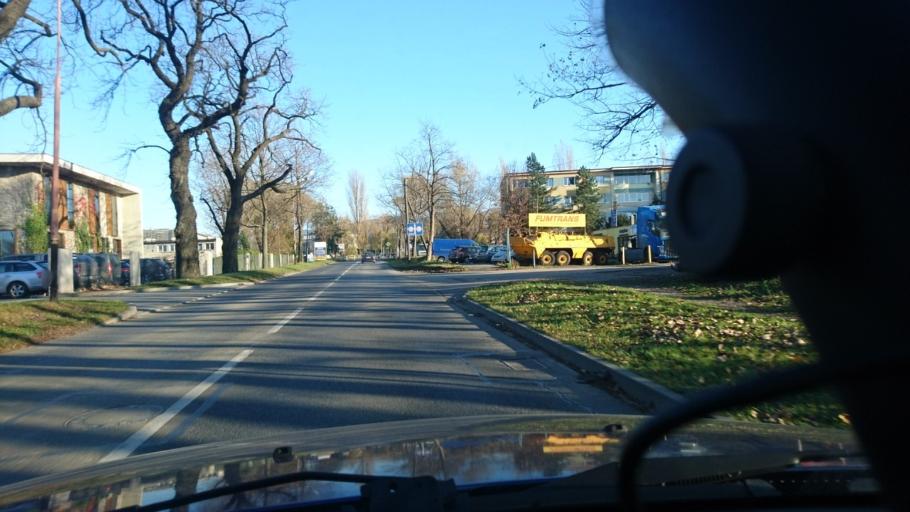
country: PL
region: Silesian Voivodeship
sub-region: Bielsko-Biala
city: Bielsko-Biala
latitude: 49.8338
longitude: 19.0612
